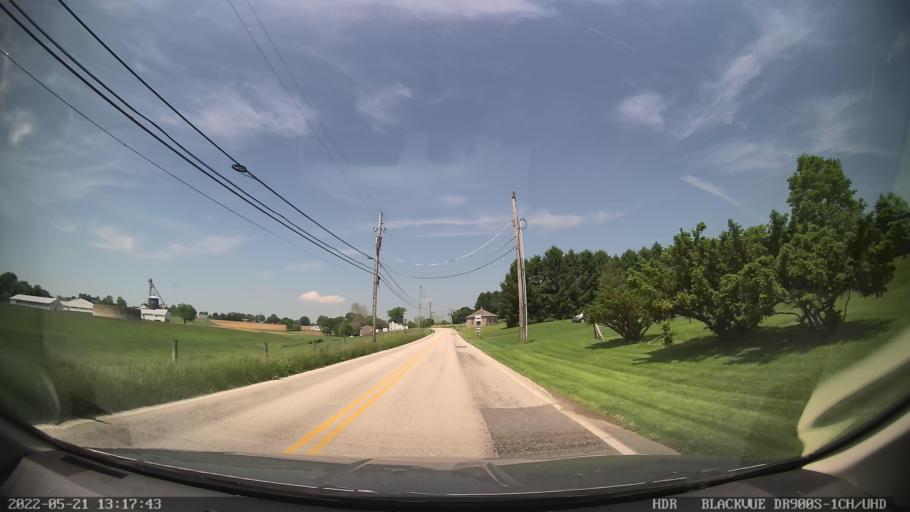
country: US
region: Pennsylvania
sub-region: Berks County
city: Bally
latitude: 40.3615
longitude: -75.5917
